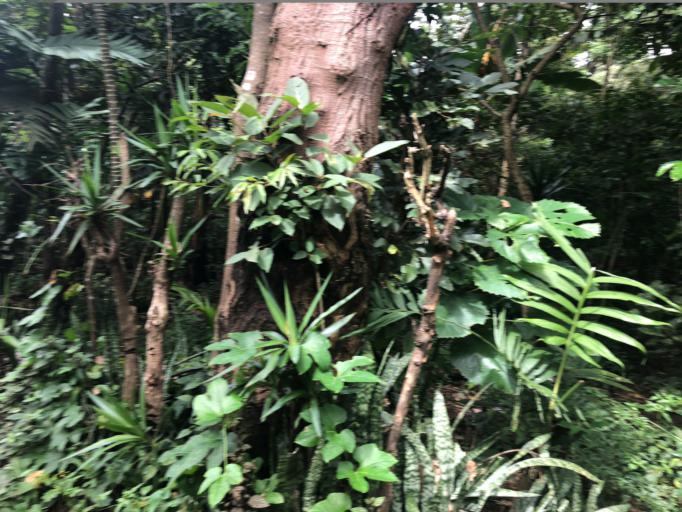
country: GT
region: Escuintla
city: San Vicente Pacaya
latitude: 14.3317
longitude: -90.6031
